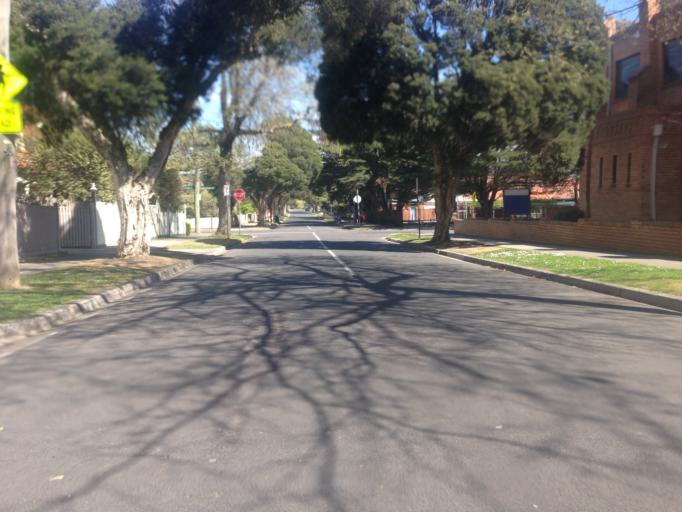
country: AU
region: Victoria
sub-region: Boroondara
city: Kew East
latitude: -37.7953
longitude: 145.0504
